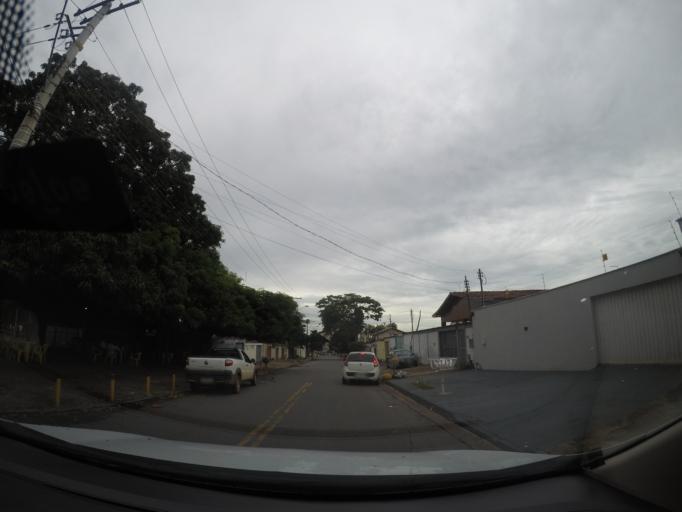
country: BR
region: Goias
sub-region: Goiania
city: Goiania
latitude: -16.6760
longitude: -49.2352
